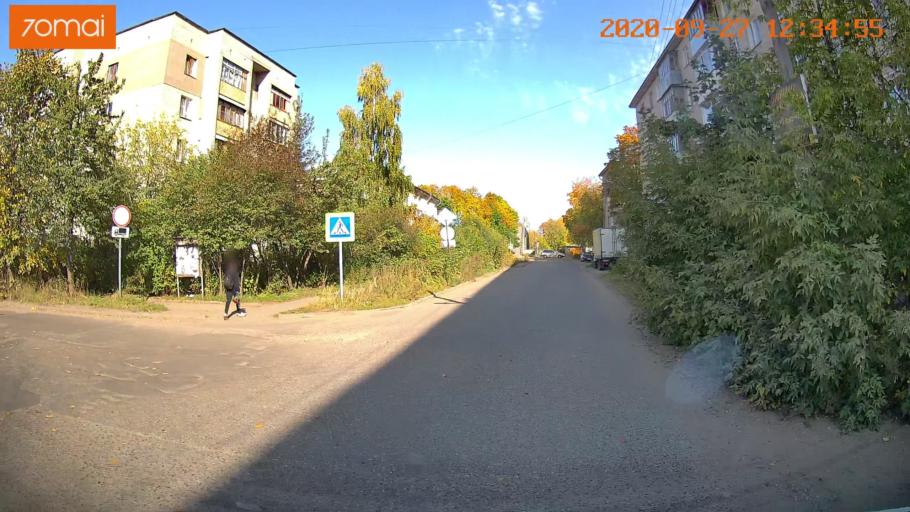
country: RU
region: Ivanovo
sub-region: Gorod Ivanovo
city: Ivanovo
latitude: 57.0179
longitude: 40.9741
